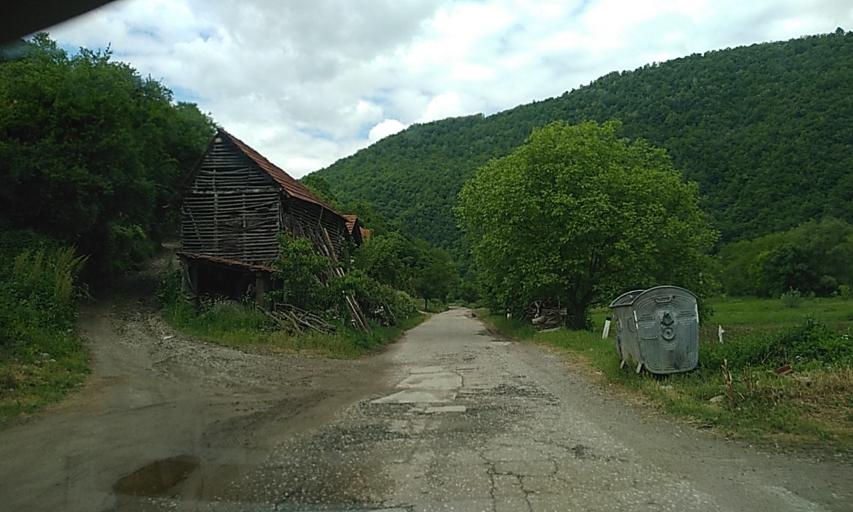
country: RS
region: Central Serbia
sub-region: Pcinjski Okrug
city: Vladicin Han
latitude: 42.7281
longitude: 22.0631
